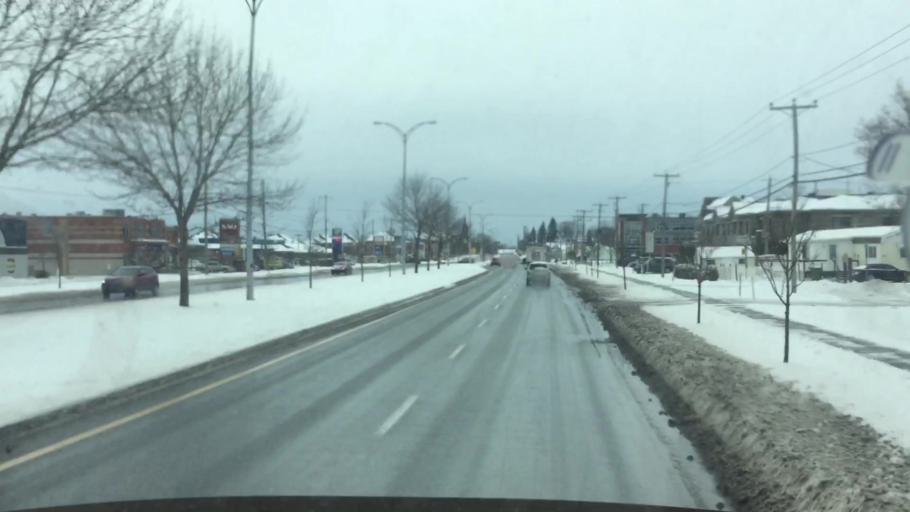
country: CA
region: Quebec
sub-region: Monteregie
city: Saint-Jean-sur-Richelieu
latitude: 45.3544
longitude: -73.2956
